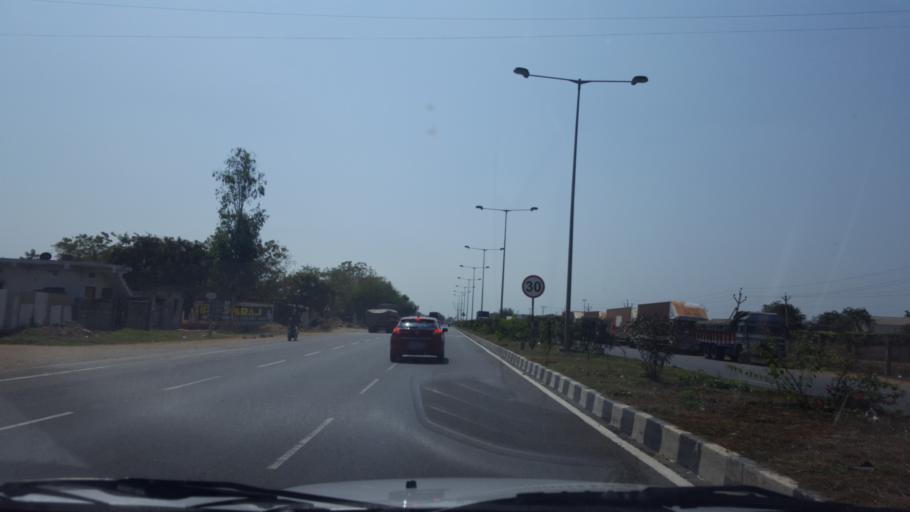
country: IN
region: Andhra Pradesh
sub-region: Prakasam
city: Addanki
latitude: 15.6887
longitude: 80.0185
